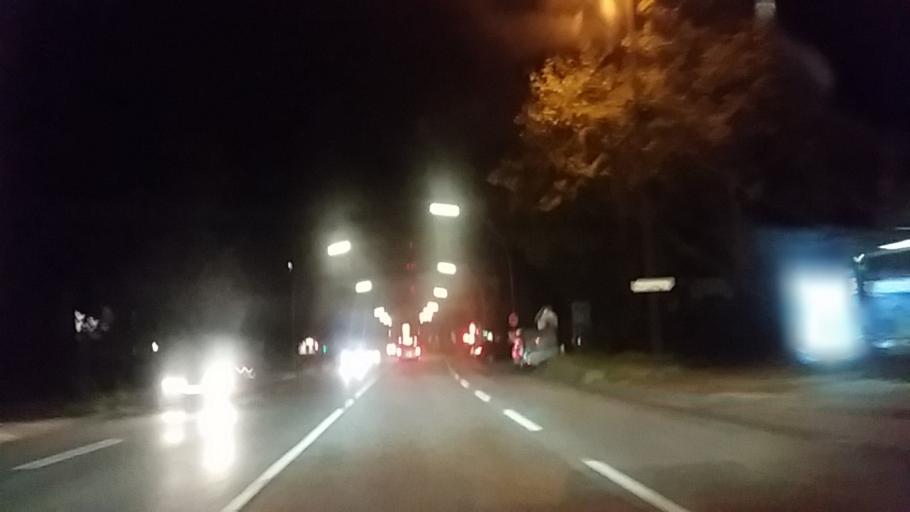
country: DE
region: Hamburg
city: Bergedorf
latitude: 53.4881
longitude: 10.1859
